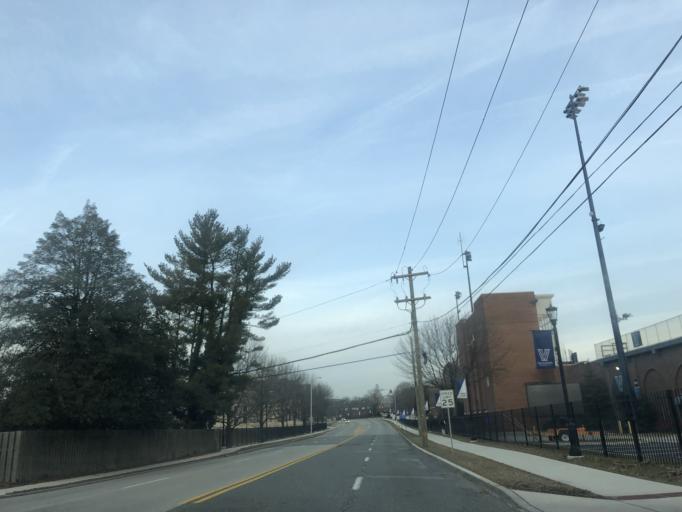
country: US
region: Pennsylvania
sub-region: Delaware County
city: Radnor
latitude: 40.0319
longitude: -75.3365
